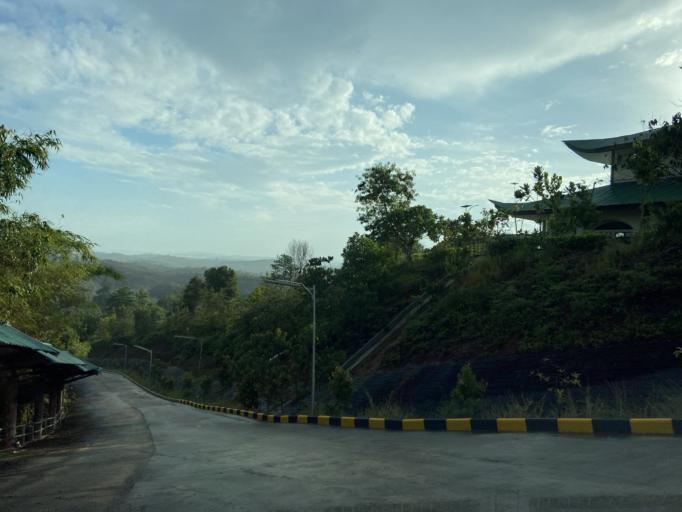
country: ID
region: Riau Islands
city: Tanjungpinang
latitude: 0.8920
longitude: 104.1229
